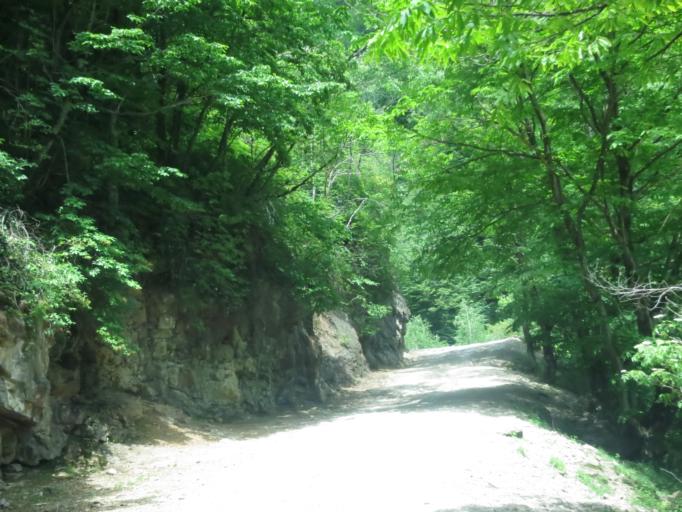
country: GE
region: Kakheti
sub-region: Telavi
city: Telavi
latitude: 42.2160
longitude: 45.4754
